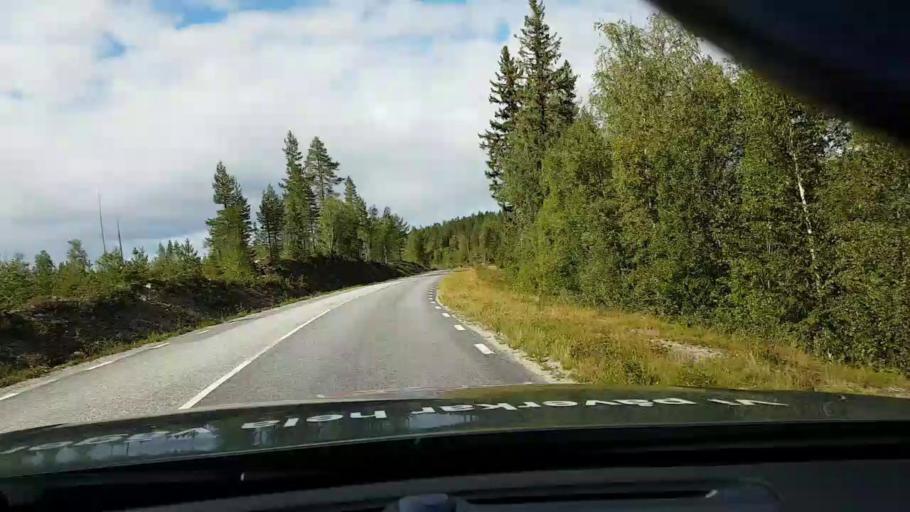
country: SE
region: Vaesterbotten
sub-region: Asele Kommun
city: Asele
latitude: 63.8425
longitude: 17.4247
